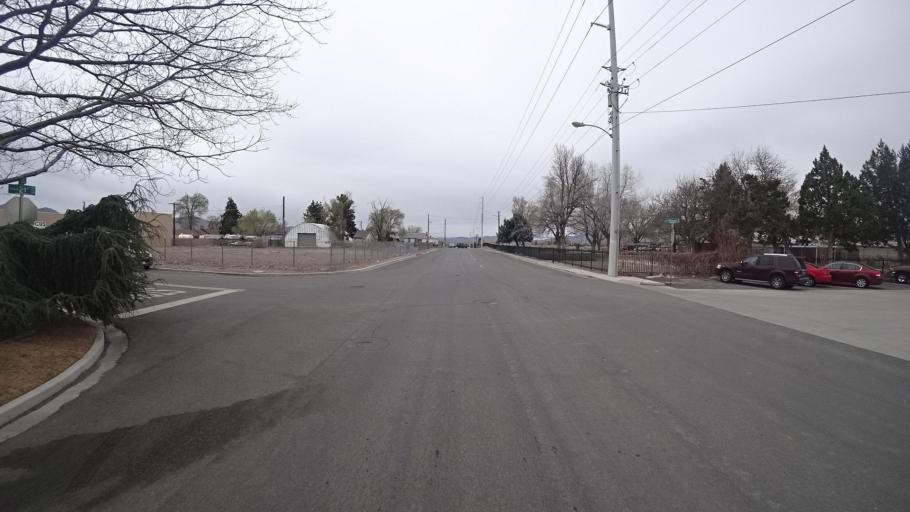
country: US
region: Nevada
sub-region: Washoe County
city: Sparks
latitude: 39.5323
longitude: -119.7714
